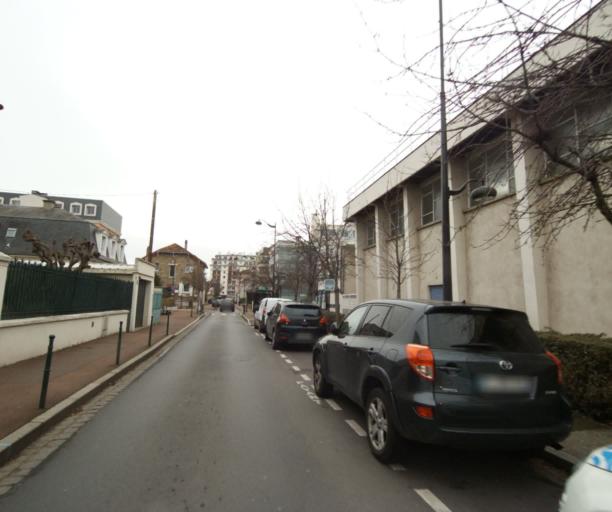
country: FR
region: Ile-de-France
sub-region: Departement des Hauts-de-Seine
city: Rueil-Malmaison
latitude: 48.8800
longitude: 2.1756
